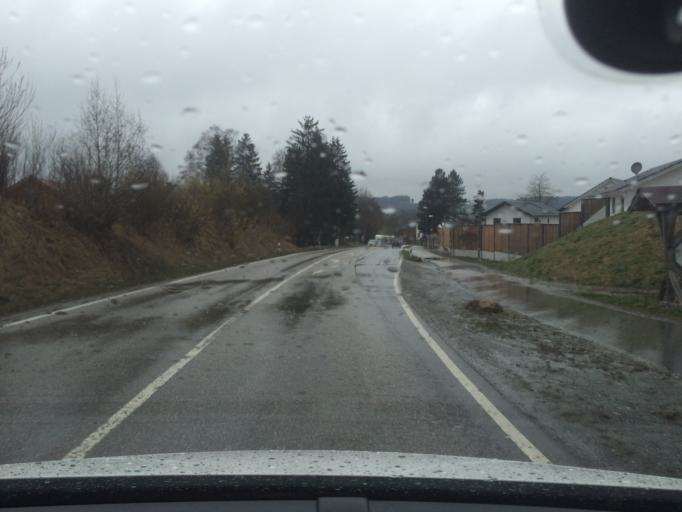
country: DE
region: Bavaria
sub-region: Upper Bavaria
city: Glonn
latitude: 47.9856
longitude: 11.8758
